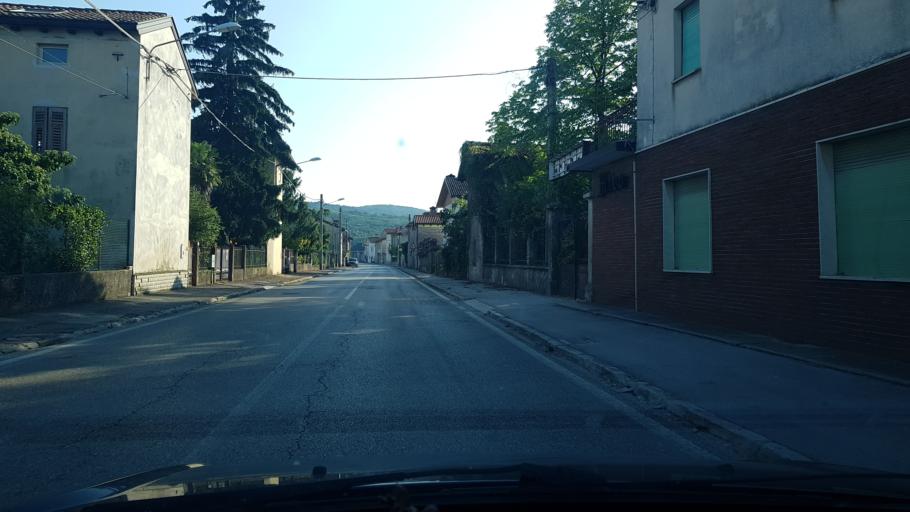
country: IT
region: Friuli Venezia Giulia
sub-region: Provincia di Gorizia
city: Savogna d'Isonzo
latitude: 45.9067
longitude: 13.5760
